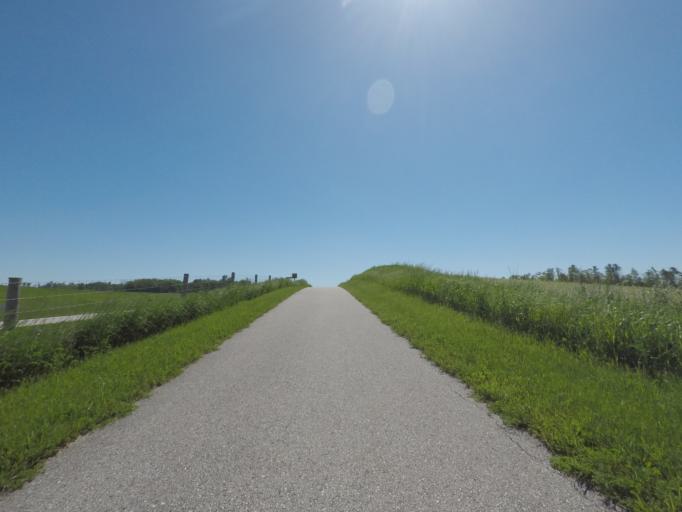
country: US
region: Wisconsin
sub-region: Sheboygan County
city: Sheboygan Falls
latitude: 43.7505
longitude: -87.8362
